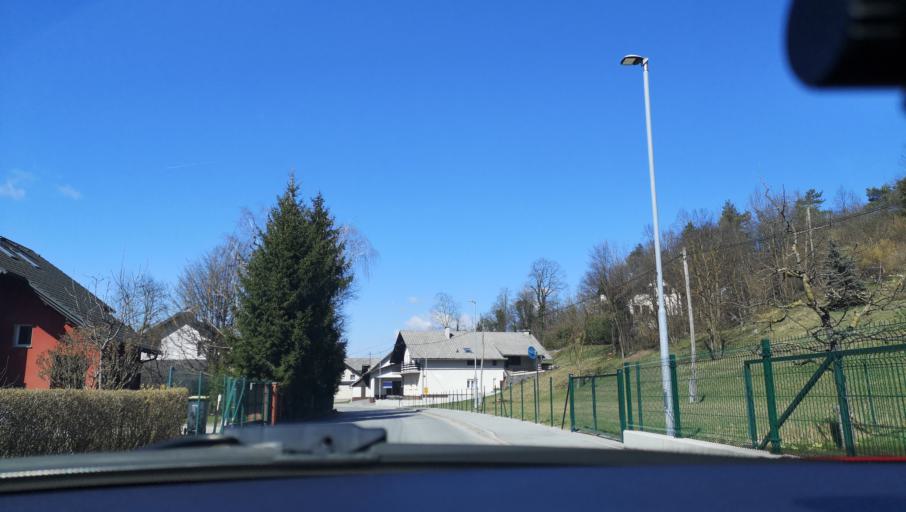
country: SI
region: Ig
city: Ig
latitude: 45.9421
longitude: 14.5116
